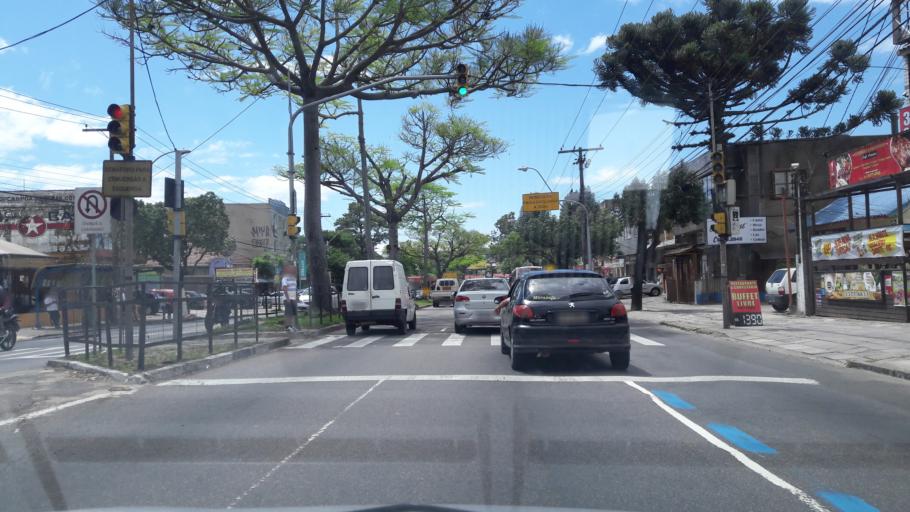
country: BR
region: Rio Grande do Sul
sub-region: Porto Alegre
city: Porto Alegre
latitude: -30.0996
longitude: -51.2313
